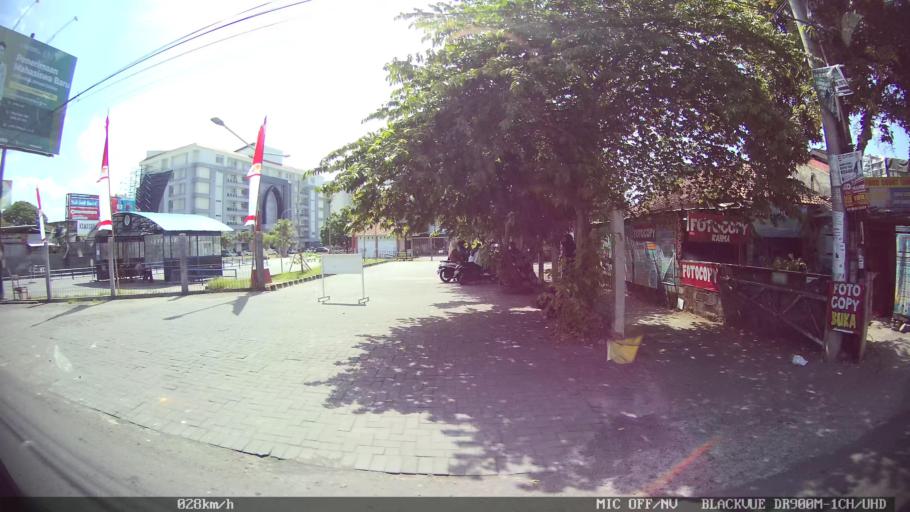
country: ID
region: Daerah Istimewa Yogyakarta
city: Sewon
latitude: -7.8342
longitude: 110.3813
